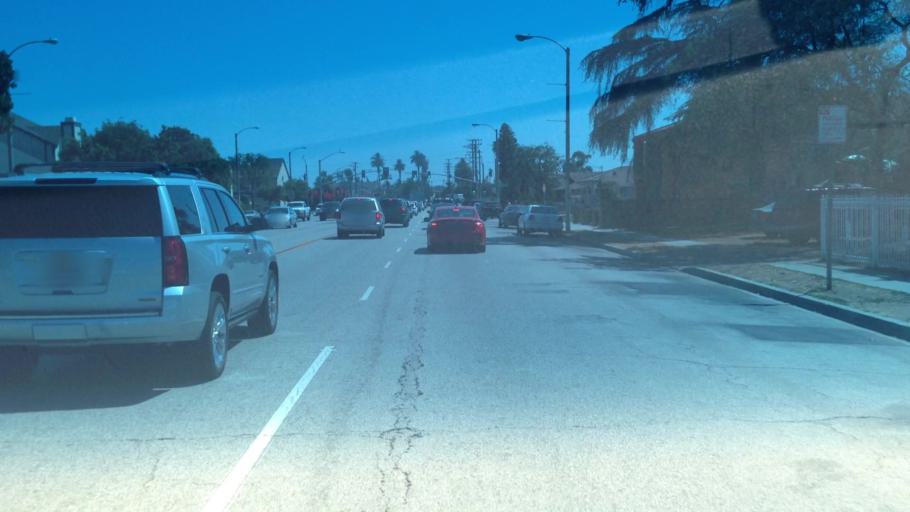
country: US
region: California
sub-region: Los Angeles County
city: Montebello
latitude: 34.0081
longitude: -118.1088
